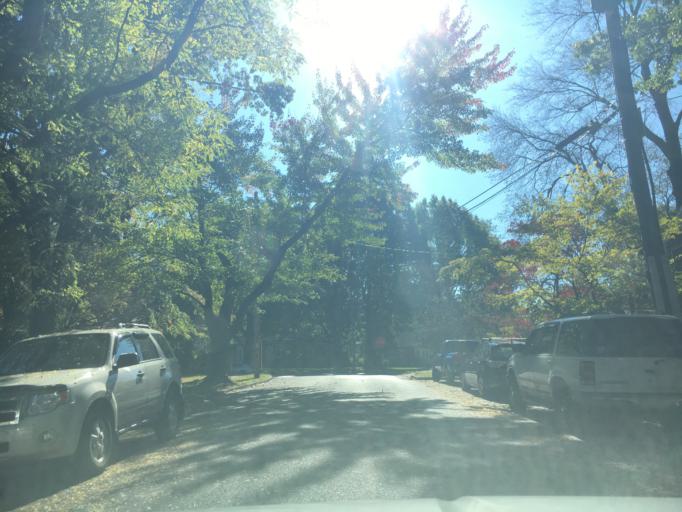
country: US
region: Pennsylvania
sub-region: Lehigh County
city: Fountain Hill
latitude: 40.6116
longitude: -75.3890
